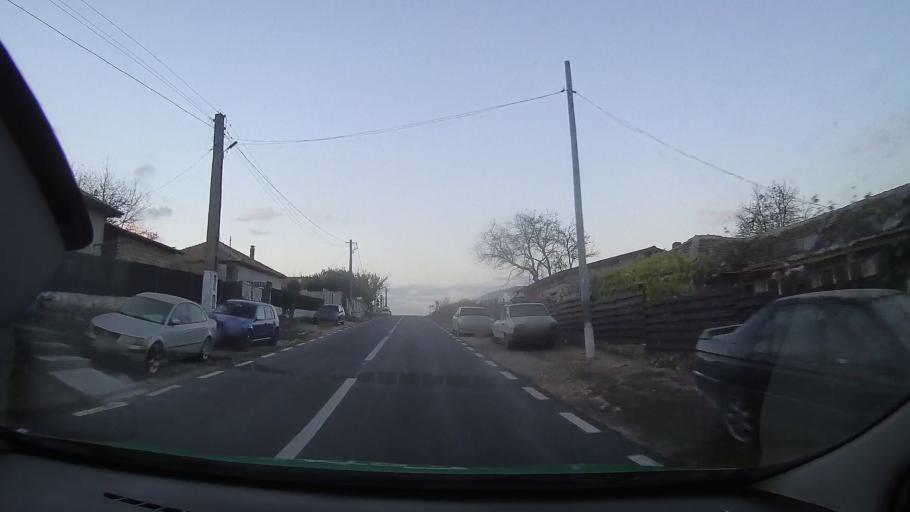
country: RO
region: Constanta
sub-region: Comuna Baneasa
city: Baneasa
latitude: 44.1019
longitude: 27.6755
